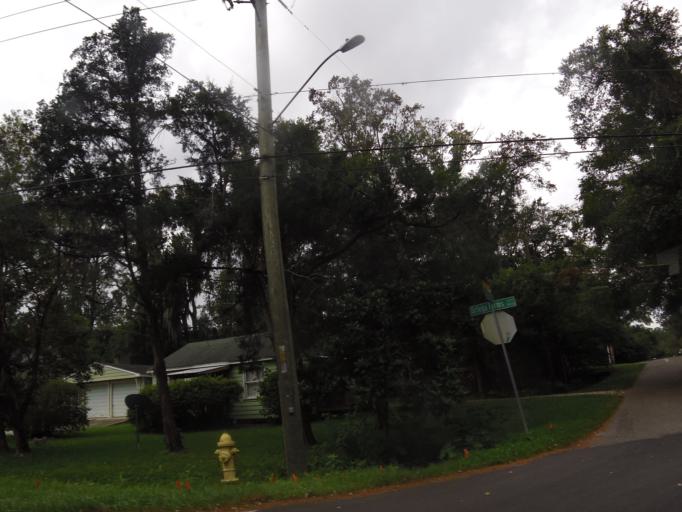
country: US
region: Florida
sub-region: Clay County
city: Bellair-Meadowbrook Terrace
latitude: 30.2504
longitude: -81.7157
